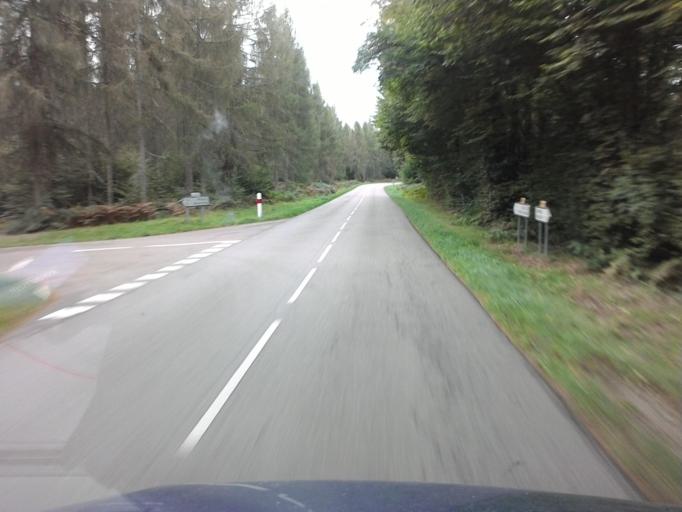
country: FR
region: Bourgogne
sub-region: Departement de la Nievre
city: Lormes
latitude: 47.2708
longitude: 3.8201
